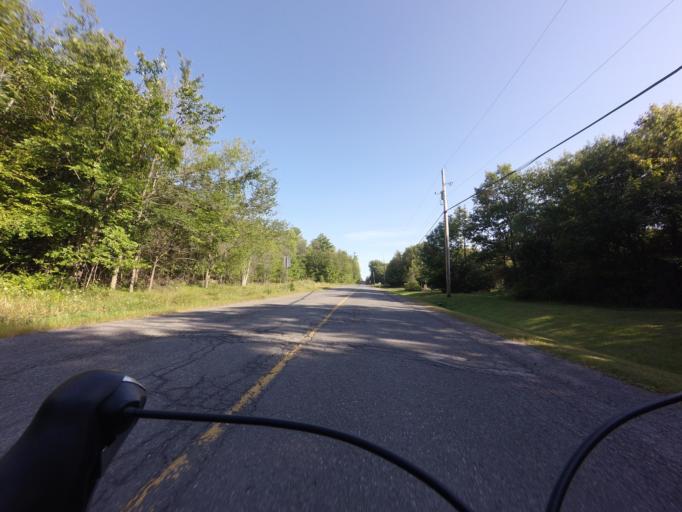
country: CA
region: Ontario
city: Bells Corners
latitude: 45.4814
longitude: -76.0455
